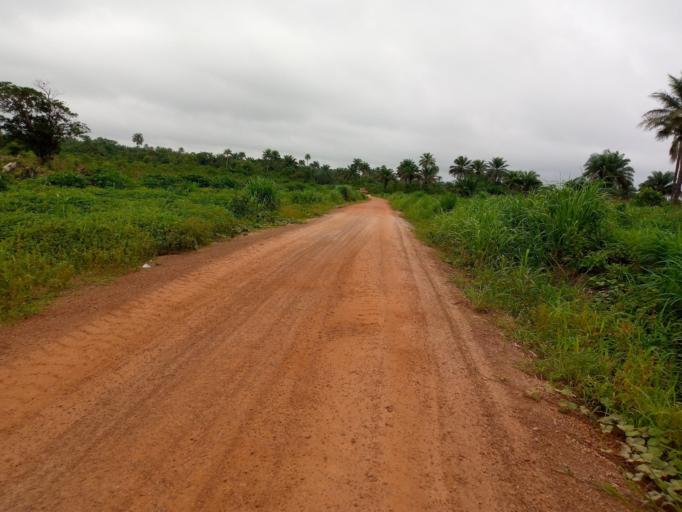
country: SL
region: Southern Province
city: Sumbuya
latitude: 7.5789
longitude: -12.0849
